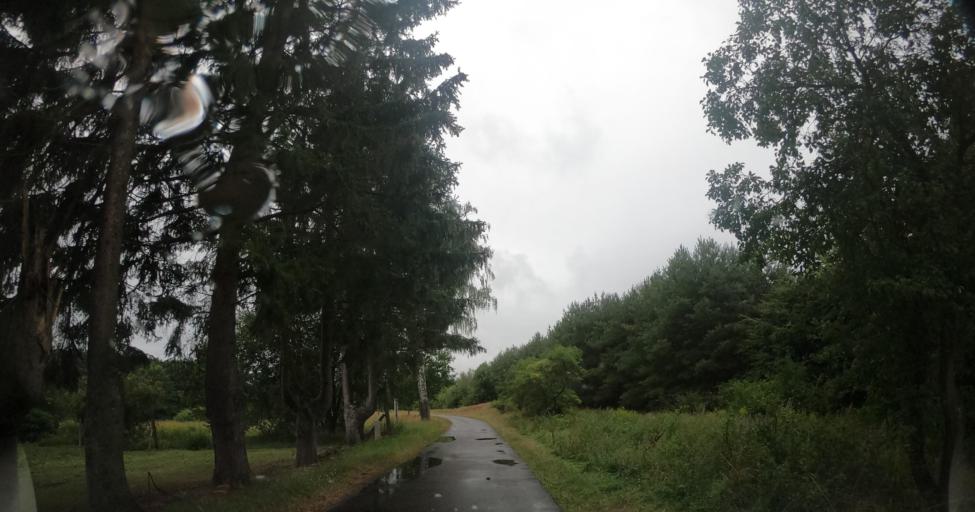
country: PL
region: West Pomeranian Voivodeship
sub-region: Powiat lobeski
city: Wegorzyno
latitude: 53.5325
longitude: 15.5012
